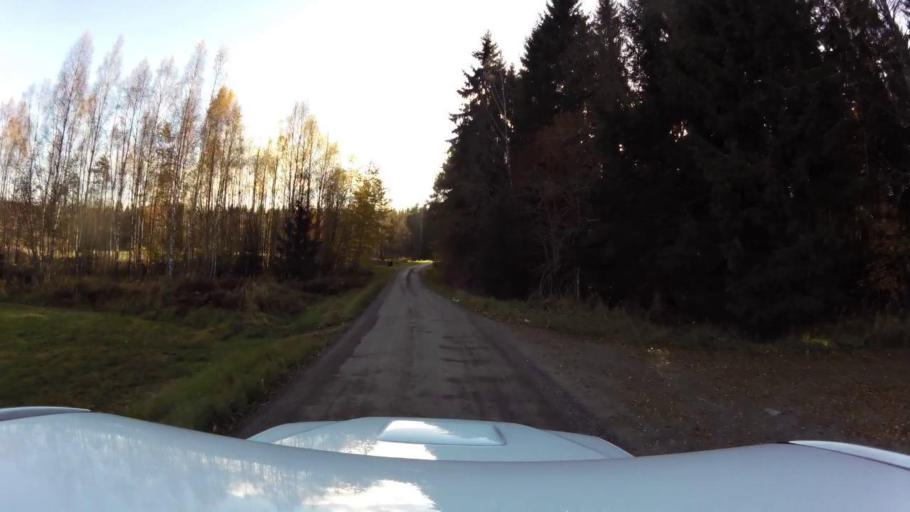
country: SE
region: OEstergoetland
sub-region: Linkopings Kommun
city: Vikingstad
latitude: 58.2157
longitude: 15.4401
